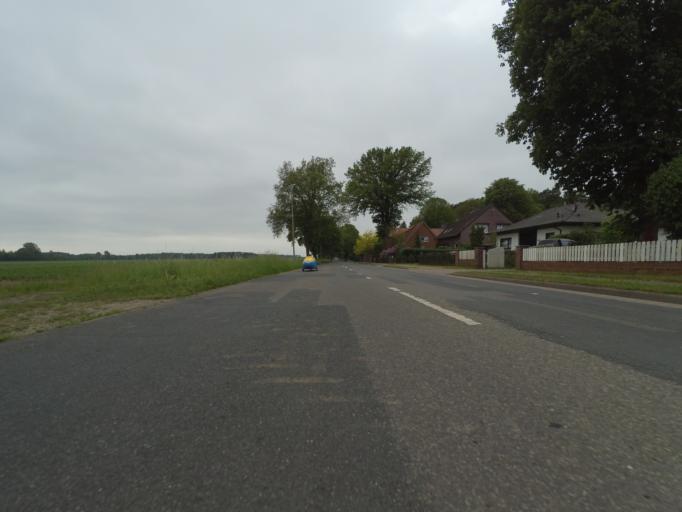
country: DE
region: Lower Saxony
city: Haenigsen
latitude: 52.4788
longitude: 10.0448
